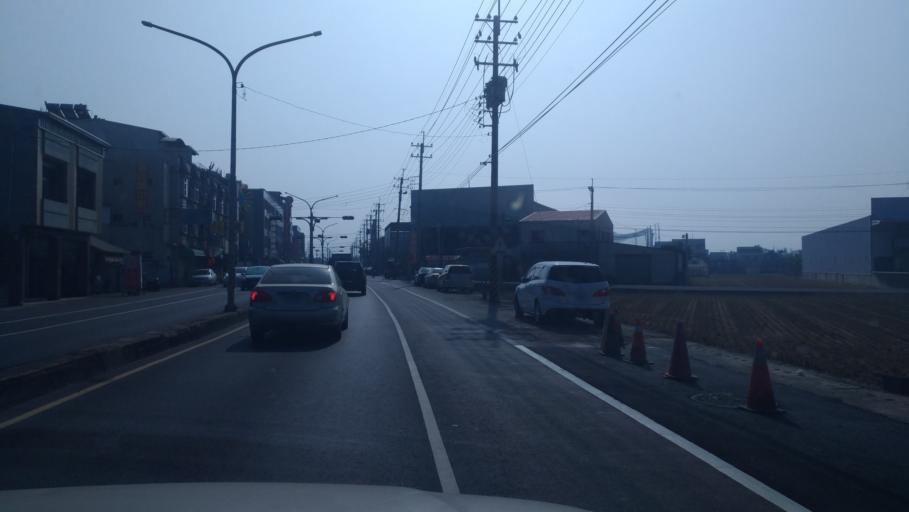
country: TW
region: Taiwan
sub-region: Chiayi
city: Jiayi Shi
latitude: 23.5164
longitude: 120.4288
